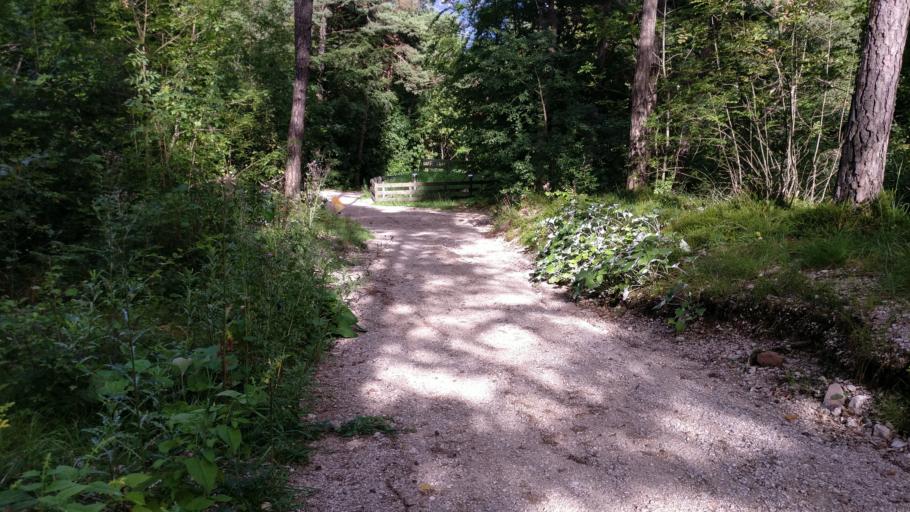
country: IT
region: Trentino-Alto Adige
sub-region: Bolzano
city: San Michele
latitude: 46.4533
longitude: 11.2287
